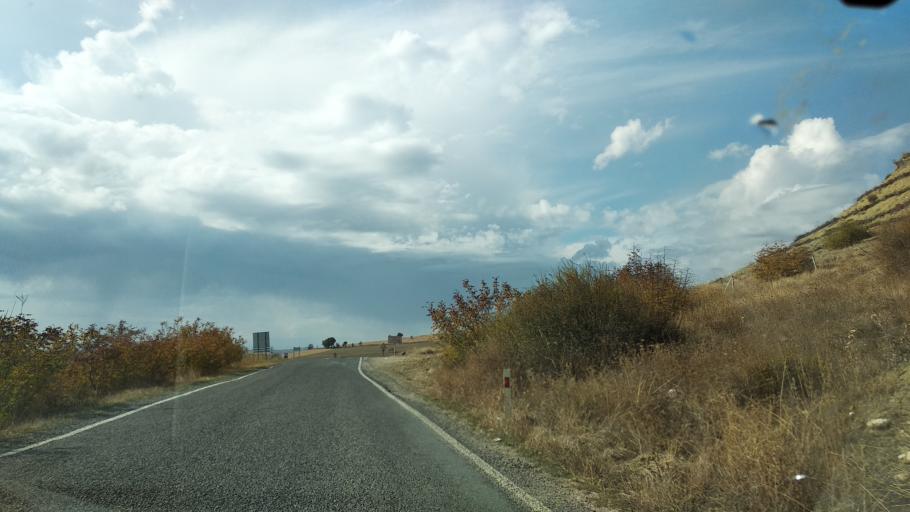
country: TR
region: Bolu
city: Seben
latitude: 40.4029
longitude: 31.5649
